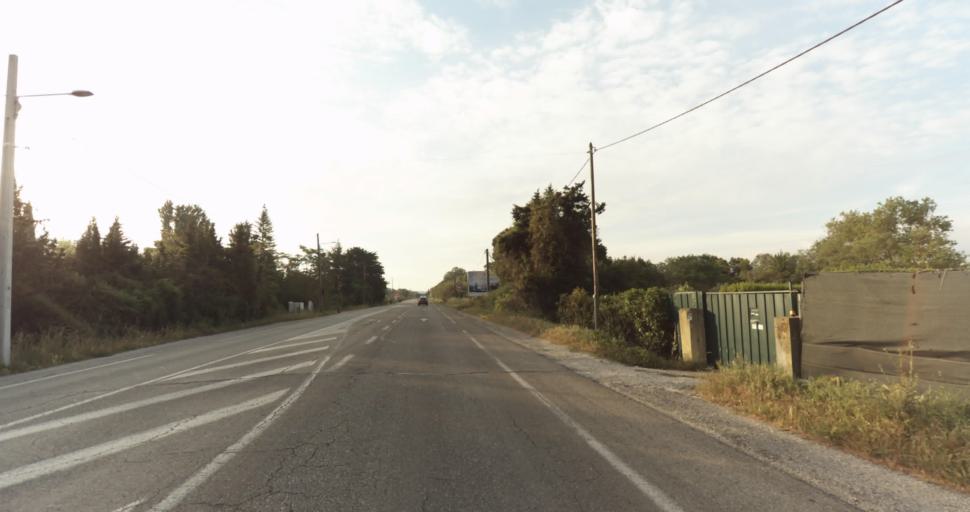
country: FR
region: Languedoc-Roussillon
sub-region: Departement du Gard
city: Caissargues
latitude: 43.8194
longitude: 4.3881
